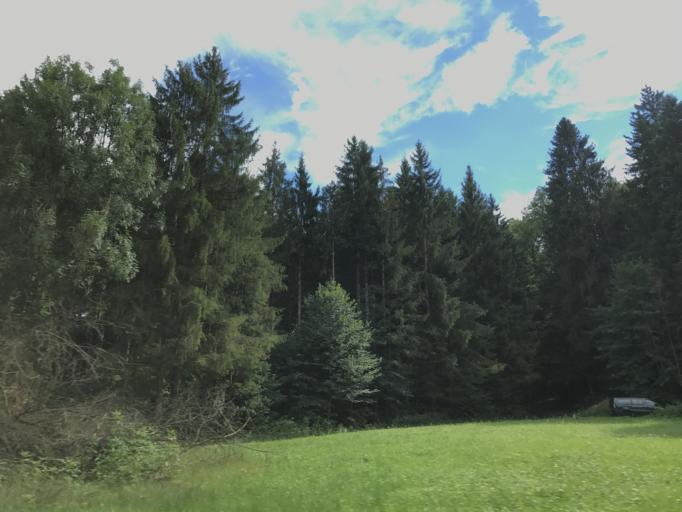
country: DE
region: Bavaria
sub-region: Swabia
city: Heimenkirch
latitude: 47.6597
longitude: 9.9170
